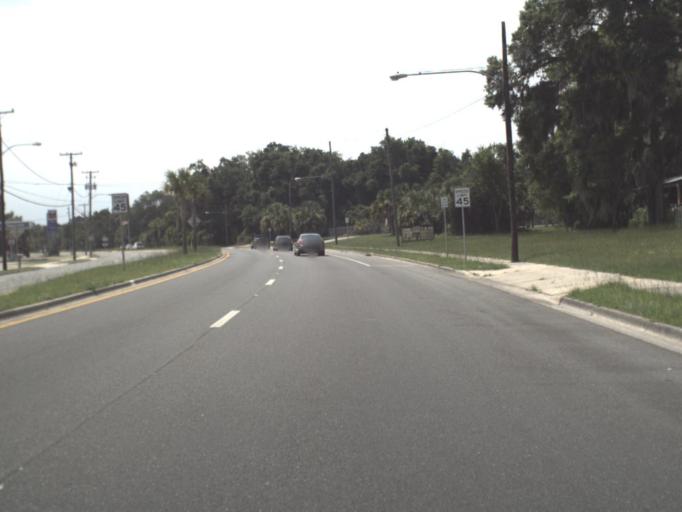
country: US
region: Florida
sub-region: Levy County
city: Chiefland
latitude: 29.4734
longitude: -82.8596
